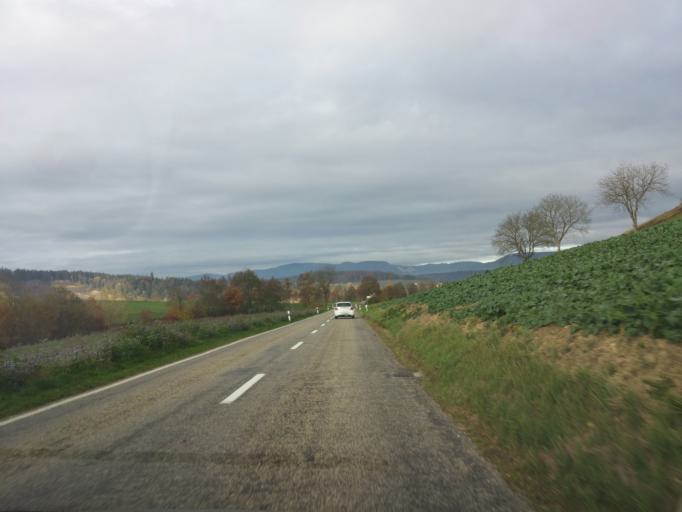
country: CH
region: Bern
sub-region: Oberaargau
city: Melchnau
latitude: 47.2204
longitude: 7.8548
